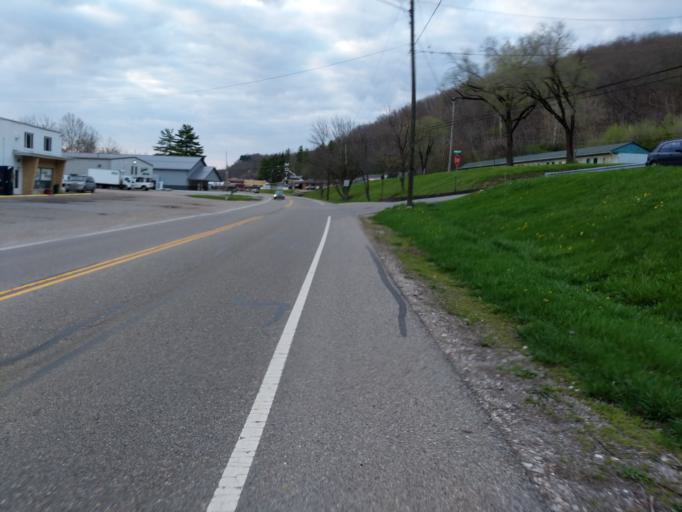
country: US
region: Ohio
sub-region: Athens County
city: Athens
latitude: 39.3490
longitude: -82.0957
